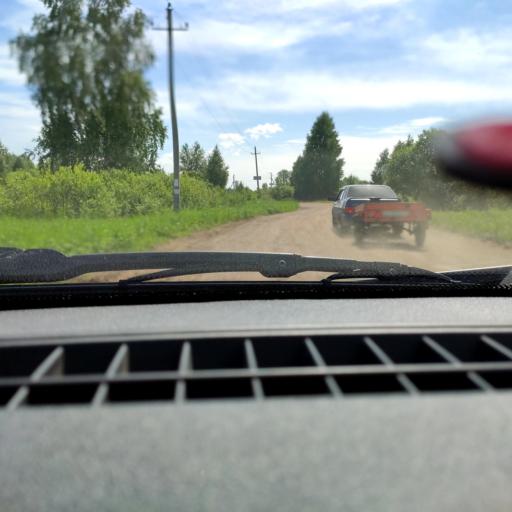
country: RU
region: Bashkortostan
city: Kabakovo
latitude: 54.7315
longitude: 56.2006
